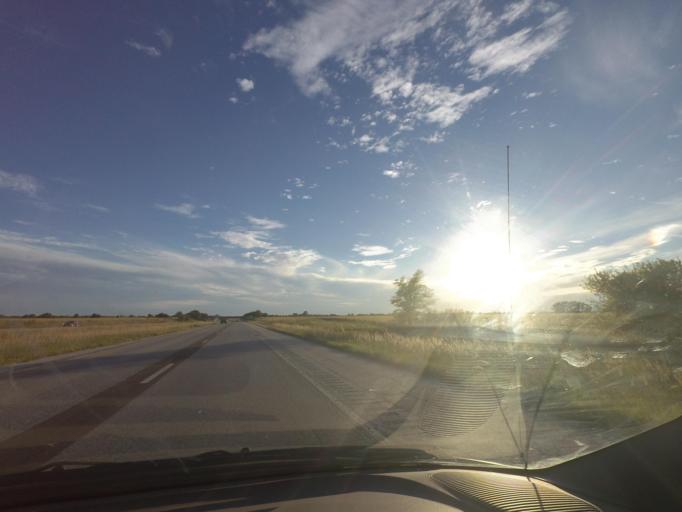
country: US
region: Illinois
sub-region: Morgan County
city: Jacksonville
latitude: 39.7322
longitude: -90.1594
